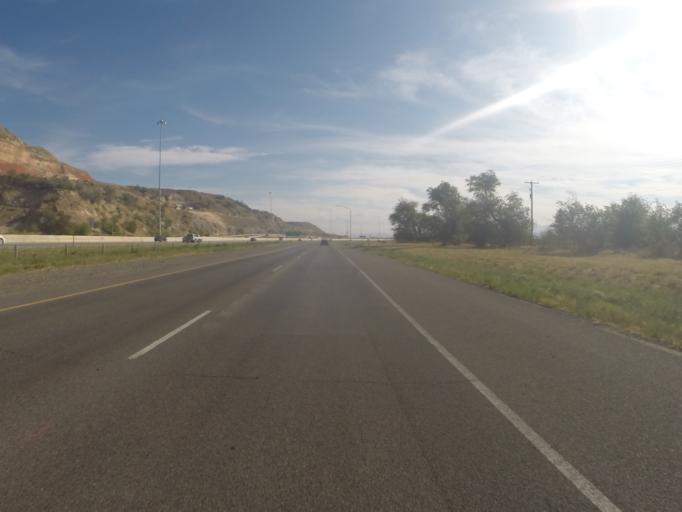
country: US
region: Utah
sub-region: Davis County
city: North Salt Lake
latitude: 40.8230
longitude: -111.9168
